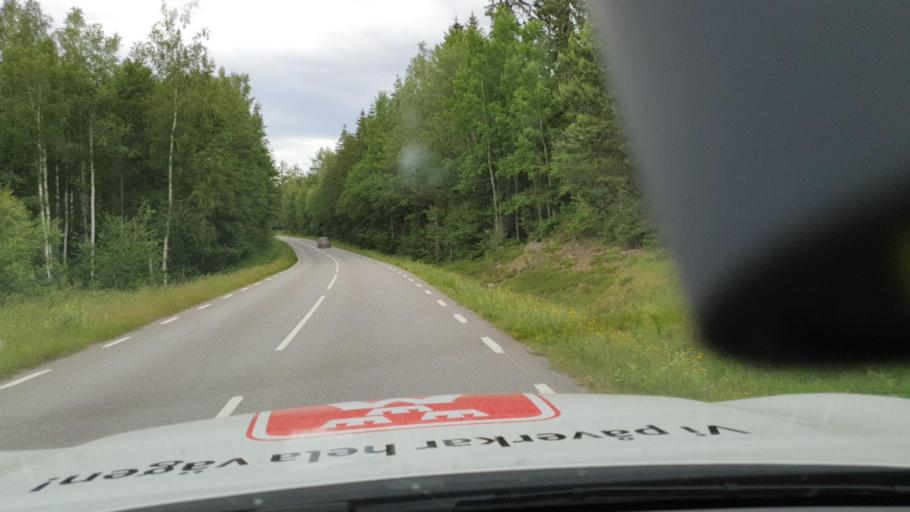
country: SE
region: Vaestra Goetaland
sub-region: Karlsborgs Kommun
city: Karlsborg
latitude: 58.7354
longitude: 14.5044
